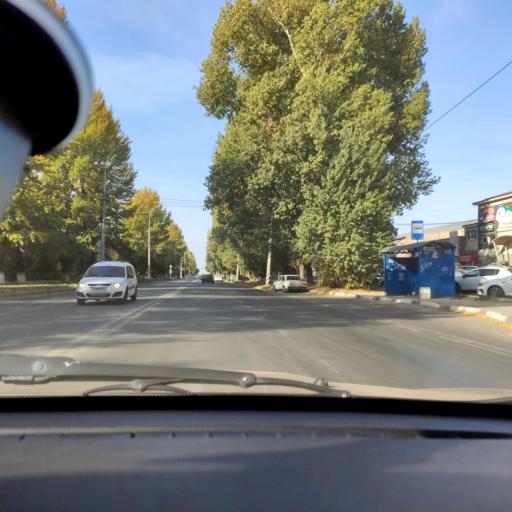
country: RU
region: Samara
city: Tol'yatti
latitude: 53.5385
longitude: 49.2735
